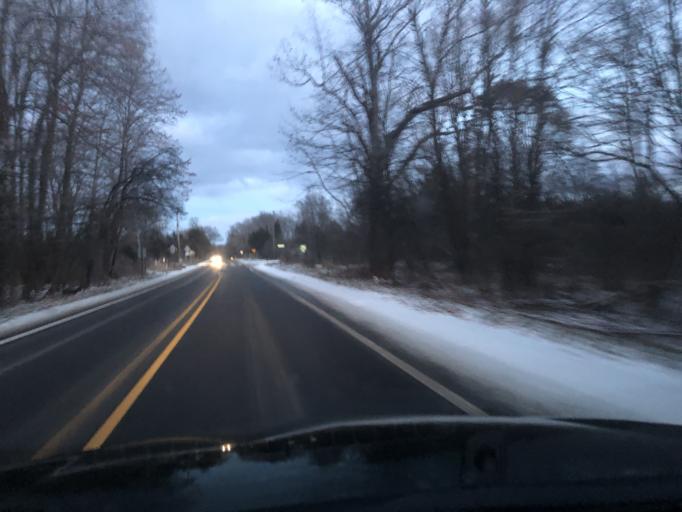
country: US
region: Michigan
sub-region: Oakland County
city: Milford
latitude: 42.5793
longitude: -83.6263
